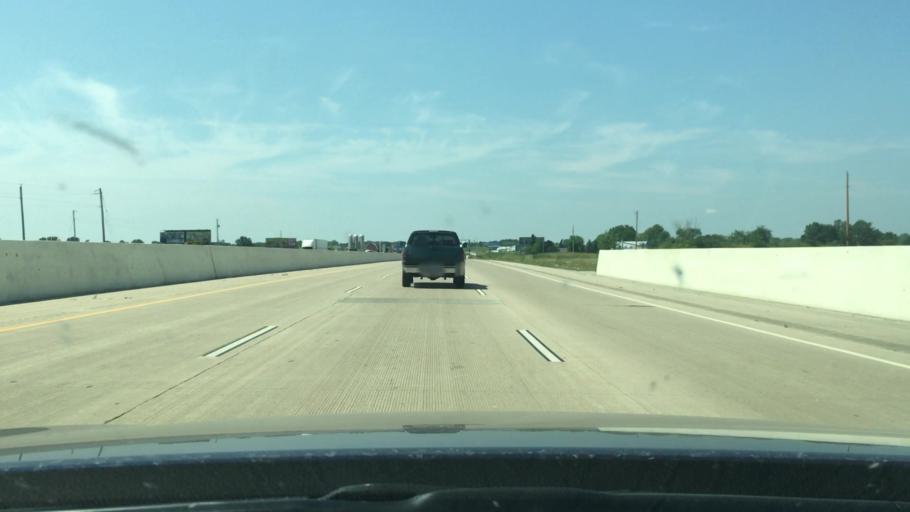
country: US
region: Wisconsin
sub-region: Winnebago County
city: Neenah
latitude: 44.1206
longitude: -88.5063
